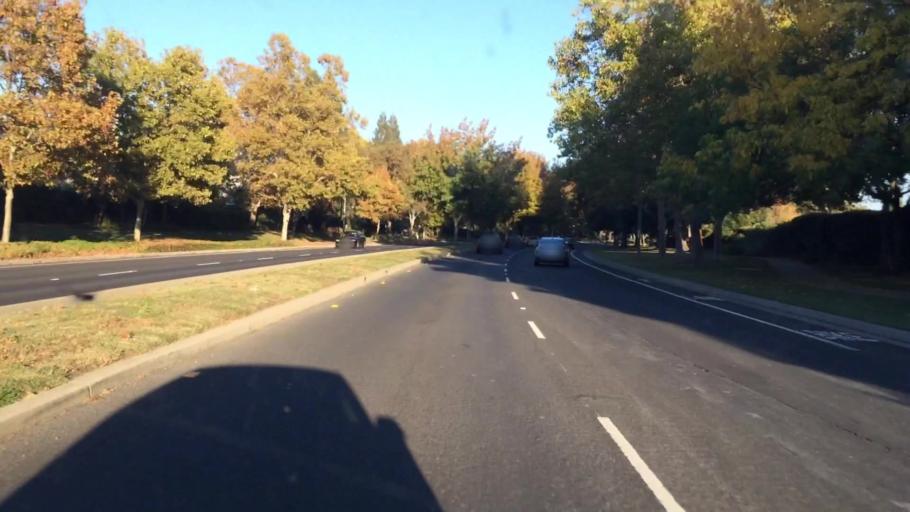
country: US
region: California
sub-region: Sacramento County
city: Laguna
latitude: 38.4359
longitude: -121.4382
